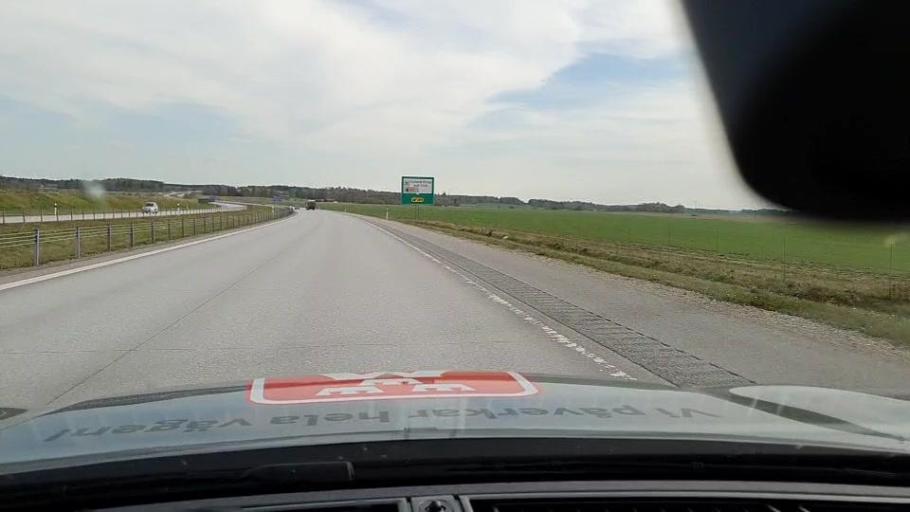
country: SE
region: Uppsala
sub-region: Uppsala Kommun
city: Storvreta
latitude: 59.9598
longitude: 17.6475
